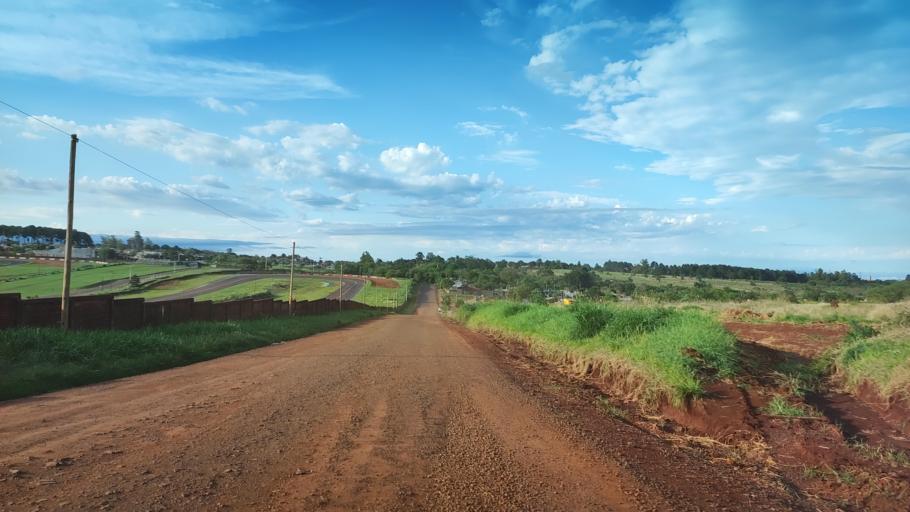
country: AR
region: Misiones
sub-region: Departamento de Capital
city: Posadas
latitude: -27.4395
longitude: -55.9243
